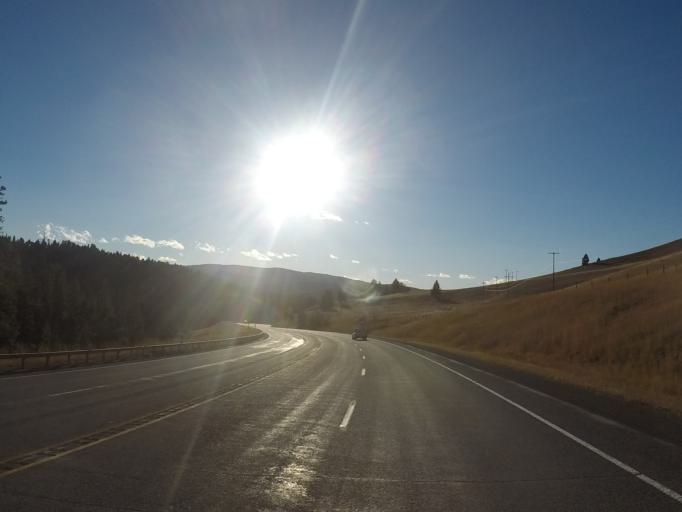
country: US
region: Montana
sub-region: Lewis and Clark County
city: Helena West Side
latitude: 46.5581
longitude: -112.3573
